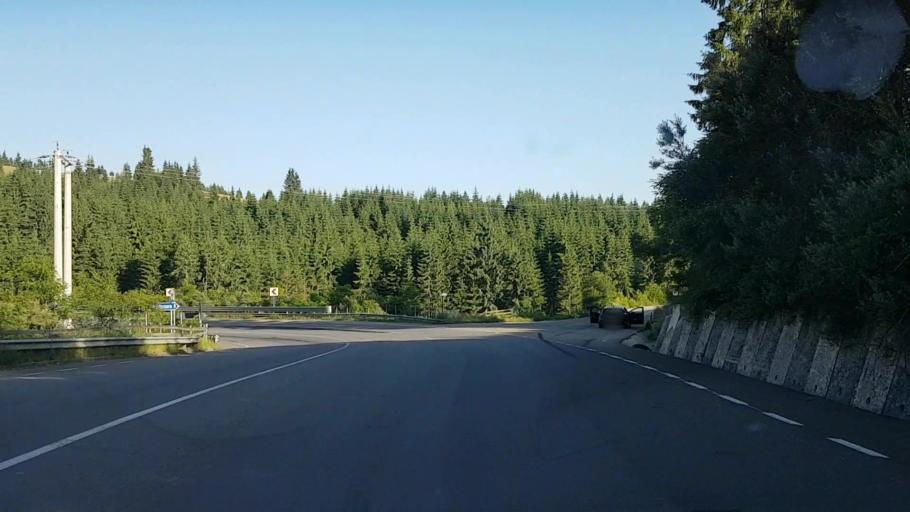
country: RO
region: Bistrita-Nasaud
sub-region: Comuna Lunca Ilvei
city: Lunca Ilvei
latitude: 47.2405
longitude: 25.0162
